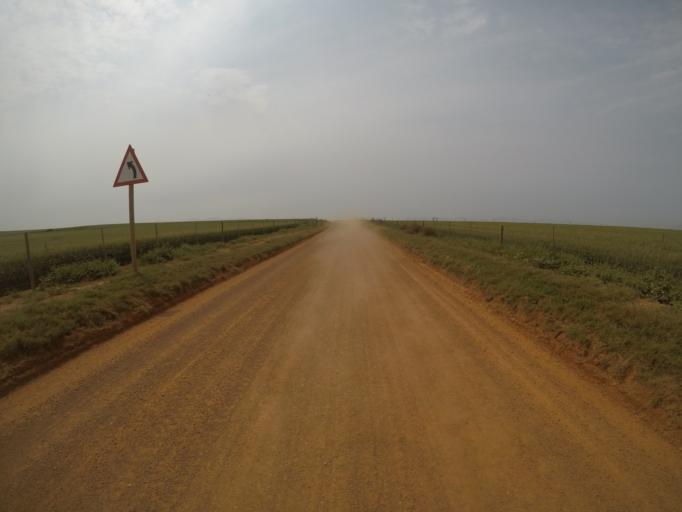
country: ZA
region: Western Cape
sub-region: City of Cape Town
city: Kraaifontein
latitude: -33.7220
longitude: 18.6737
